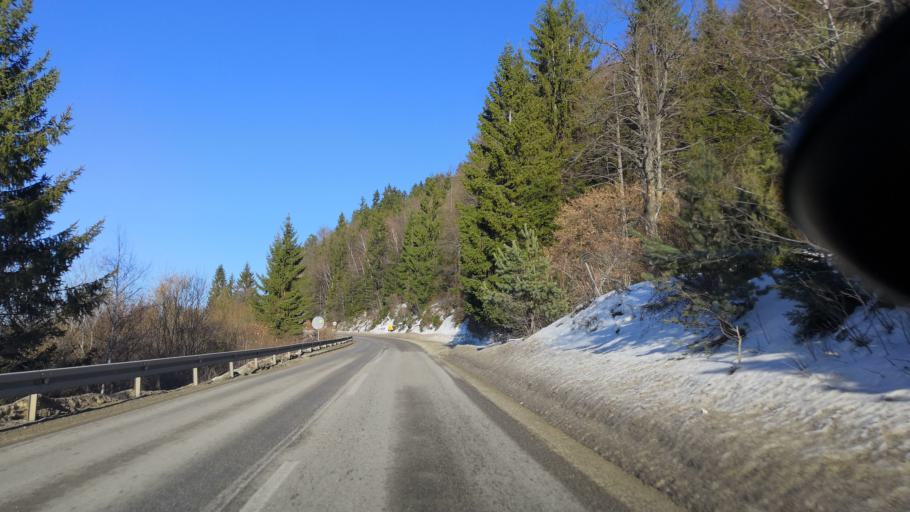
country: BA
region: Republika Srpska
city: Pale
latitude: 43.9061
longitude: 18.6372
